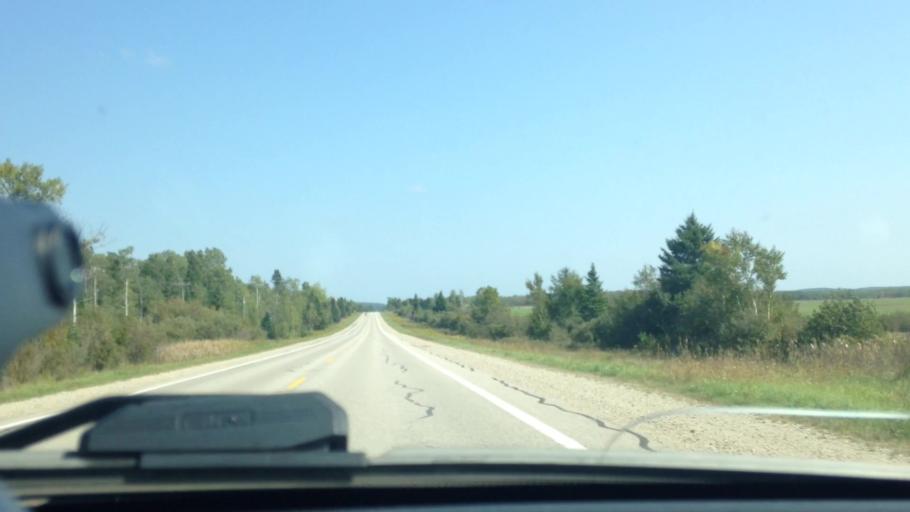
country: US
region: Michigan
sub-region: Luce County
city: Newberry
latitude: 46.3103
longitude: -85.6092
